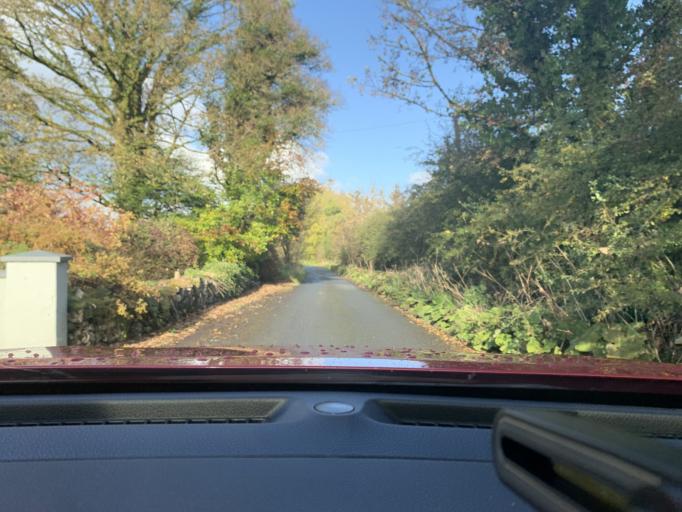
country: IE
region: Connaught
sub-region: Sligo
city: Ballymote
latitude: 54.1008
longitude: -8.4349
